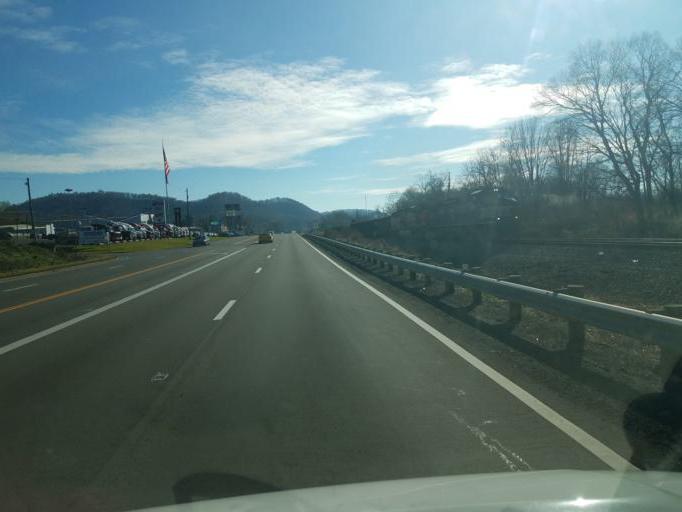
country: US
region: Ohio
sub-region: Scioto County
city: Rosemount
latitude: 38.7936
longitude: -82.9859
